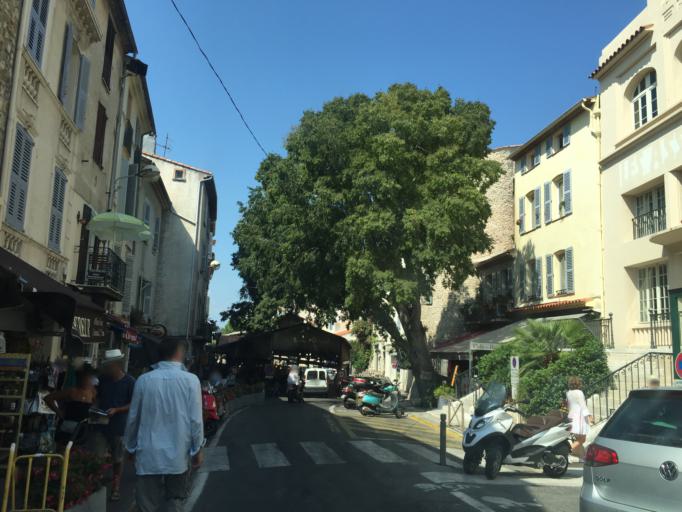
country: FR
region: Provence-Alpes-Cote d'Azur
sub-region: Departement des Alpes-Maritimes
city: Antibes
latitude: 43.5802
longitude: 7.1272
